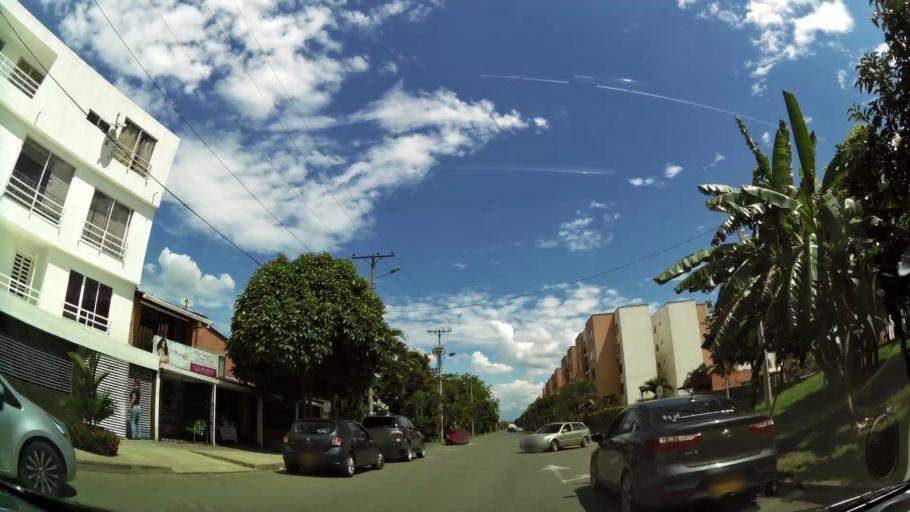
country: CO
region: Valle del Cauca
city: Cali
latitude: 3.3941
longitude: -76.5188
